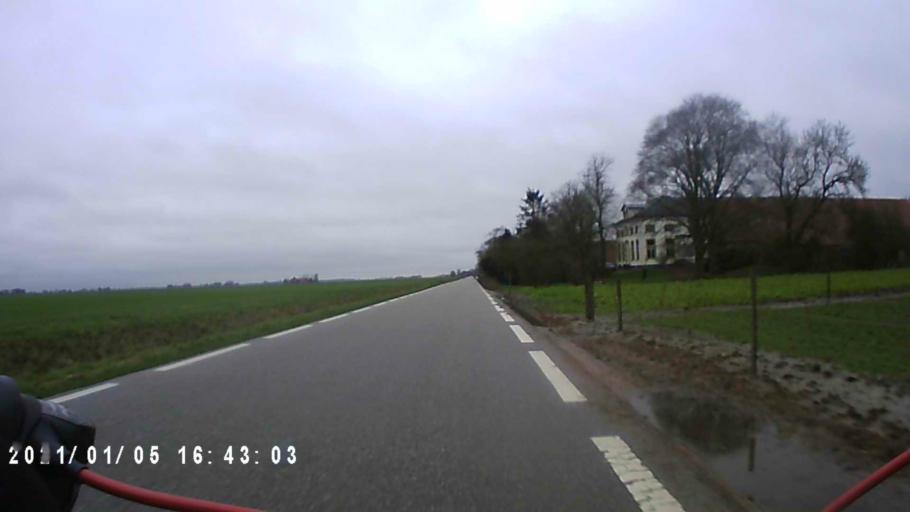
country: NL
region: Groningen
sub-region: Gemeente  Oldambt
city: Winschoten
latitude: 53.2136
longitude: 7.0512
